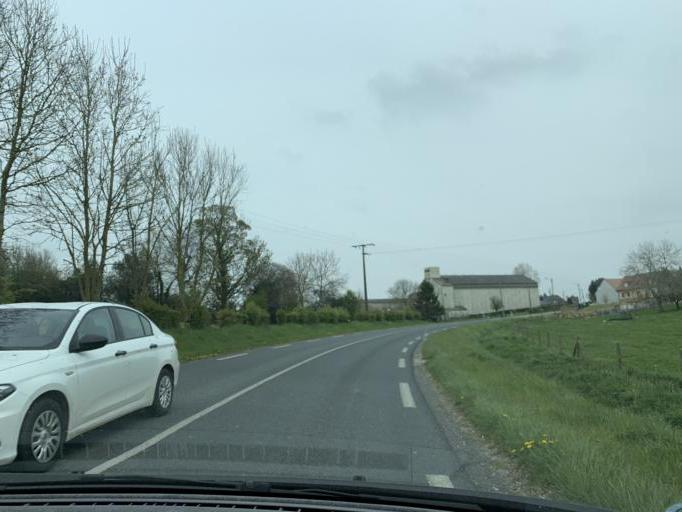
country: FR
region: Haute-Normandie
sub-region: Departement de la Seine-Maritime
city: Londinieres
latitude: 49.8436
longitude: 1.4707
